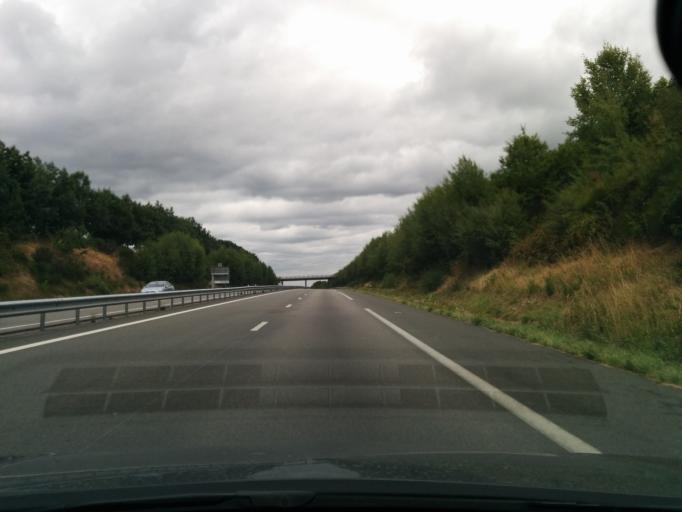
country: FR
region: Limousin
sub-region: Departement de la Haute-Vienne
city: Saint-Sulpice-les-Feuilles
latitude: 46.3253
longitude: 1.4179
